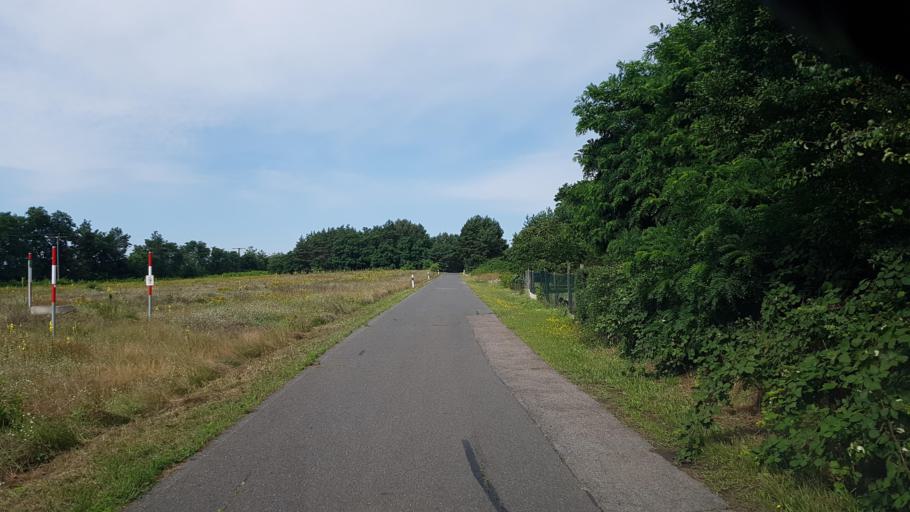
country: DE
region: Brandenburg
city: Drebkau
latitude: 51.6198
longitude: 14.2661
